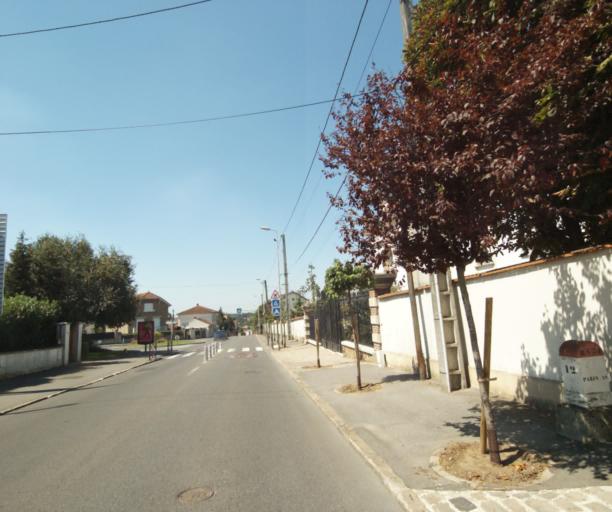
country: FR
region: Ile-de-France
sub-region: Departement de Seine-et-Marne
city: Thorigny-sur-Marne
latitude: 48.8777
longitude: 2.7175
